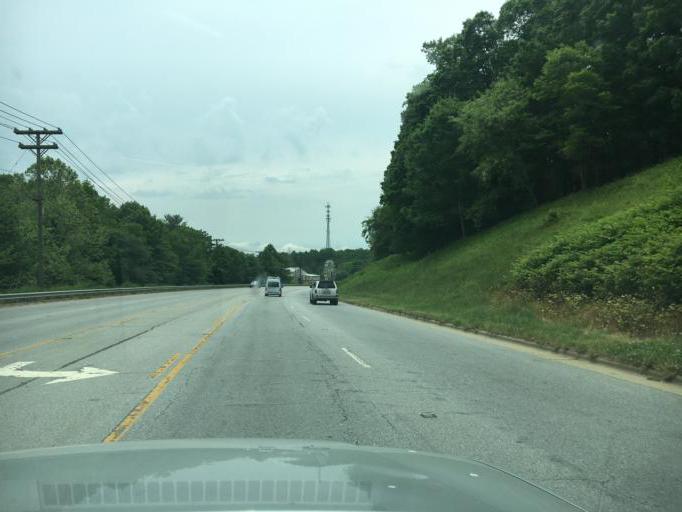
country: US
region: North Carolina
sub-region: Henderson County
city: Balfour
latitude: 35.3594
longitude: -82.4787
